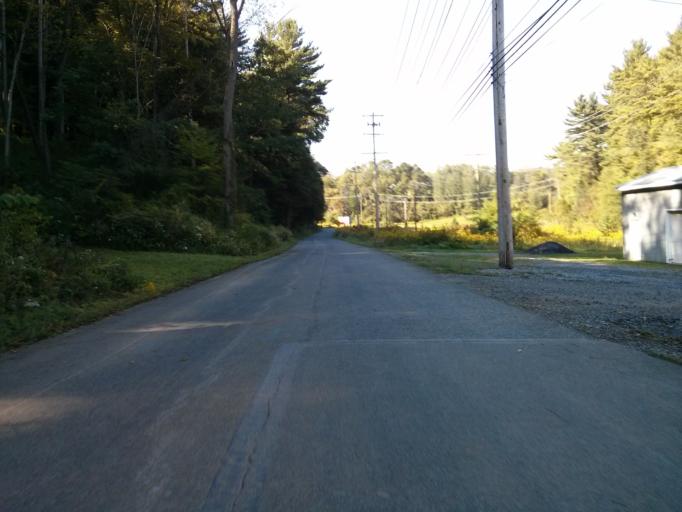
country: US
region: Pennsylvania
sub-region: Centre County
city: State College
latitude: 40.8180
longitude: -77.8735
